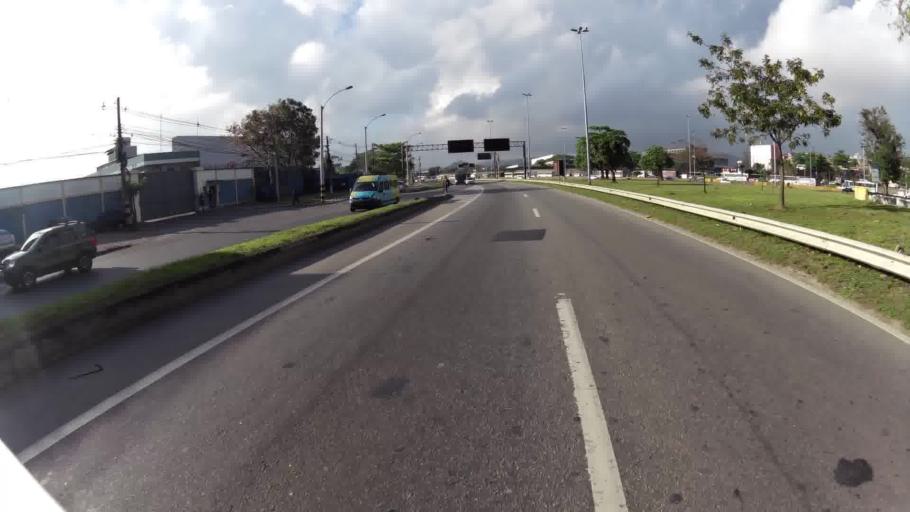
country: BR
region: Rio de Janeiro
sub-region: Duque De Caxias
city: Duque de Caxias
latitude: -22.8157
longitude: -43.2872
